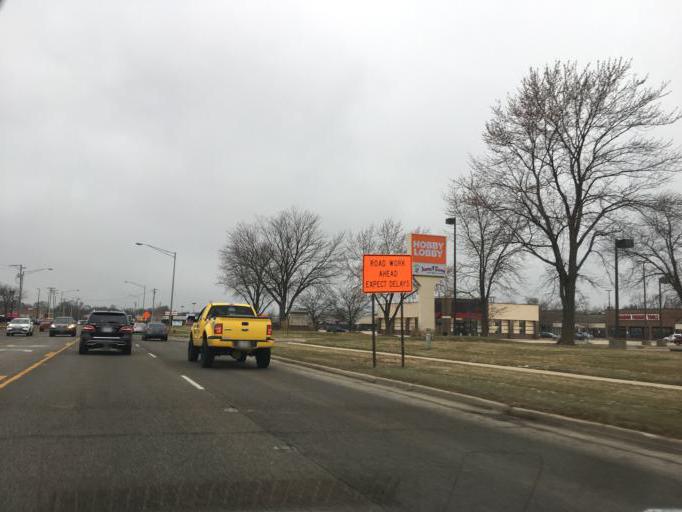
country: US
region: Illinois
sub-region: McHenry County
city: Crystal Lake
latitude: 42.2263
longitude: -88.3206
